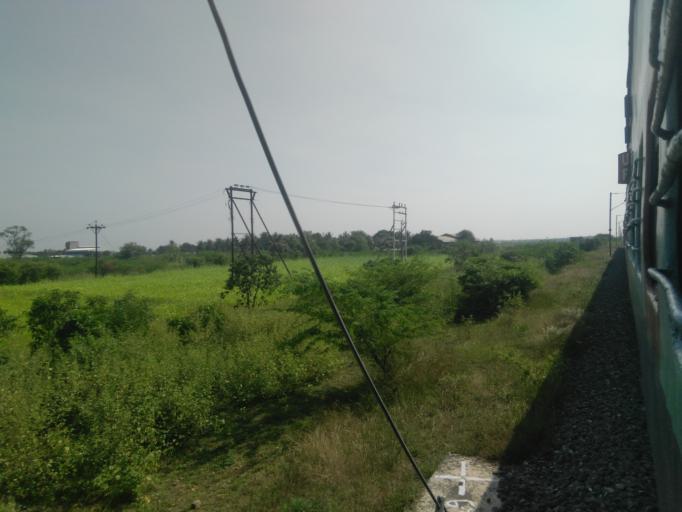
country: IN
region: Tamil Nadu
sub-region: Coimbatore
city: Periyanayakkanpalaiyam
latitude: 11.1325
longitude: 76.9487
